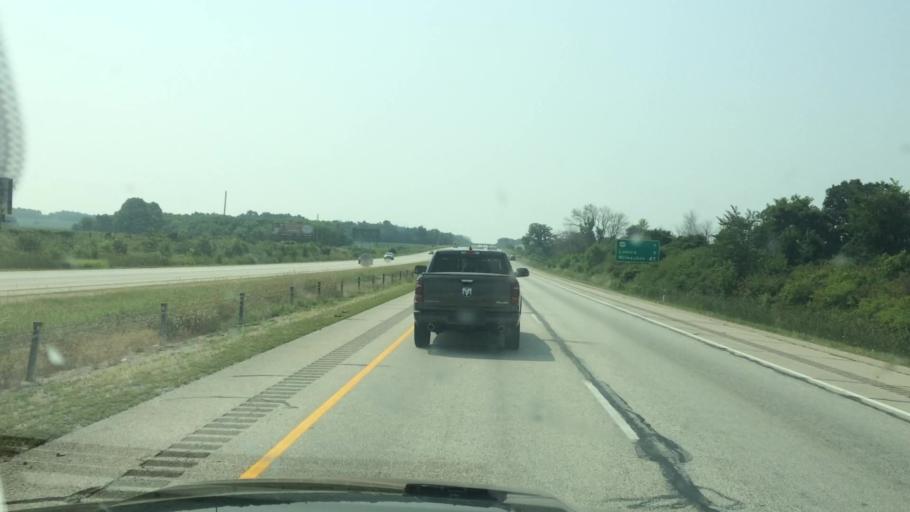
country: US
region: Wisconsin
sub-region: Fond du Lac County
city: Fond du Lac
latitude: 43.7228
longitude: -88.4425
